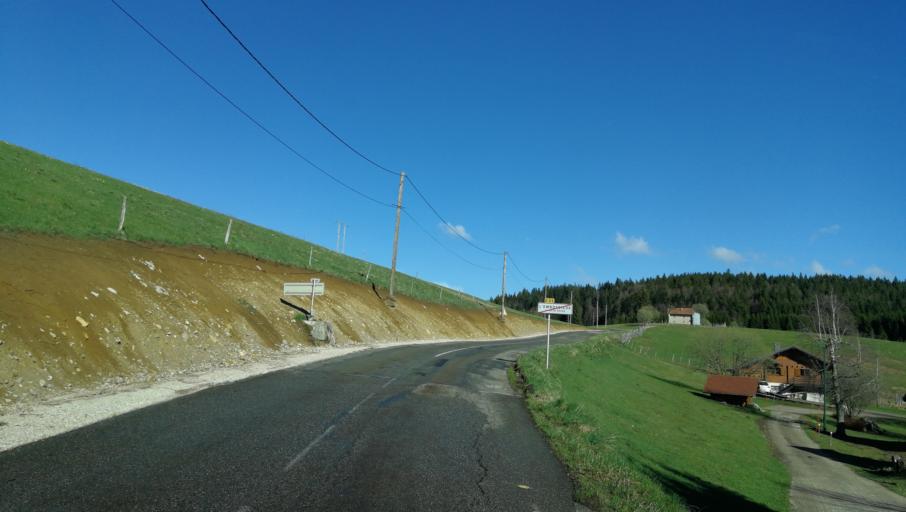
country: FR
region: Franche-Comte
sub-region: Departement du Jura
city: Saint-Claude
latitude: 46.2982
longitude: 5.8575
